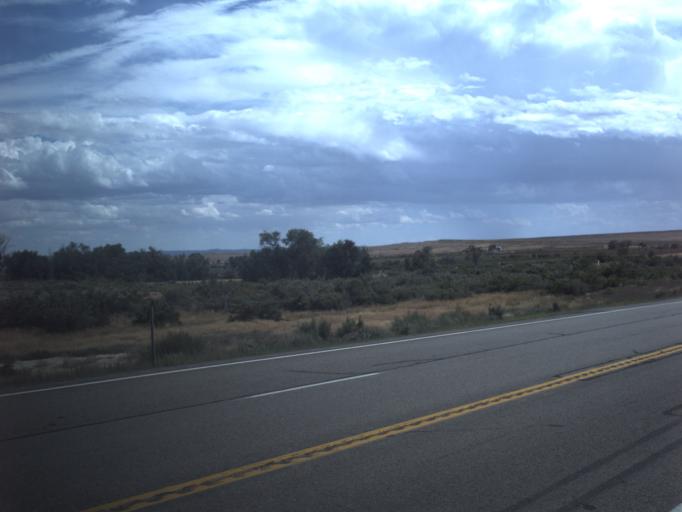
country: US
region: Utah
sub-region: Carbon County
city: Price
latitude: 39.5262
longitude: -110.8223
